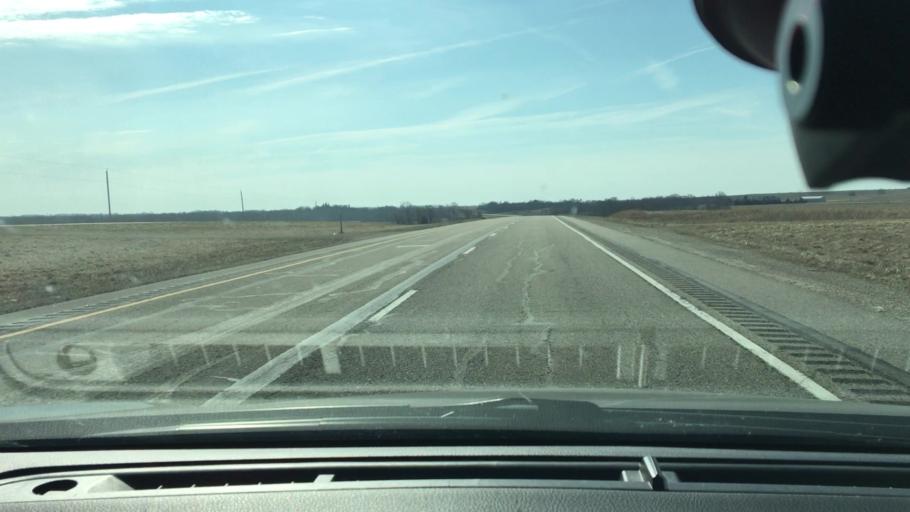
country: US
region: Iowa
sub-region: Chickasaw County
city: Nashua
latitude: 42.9876
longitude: -92.5888
